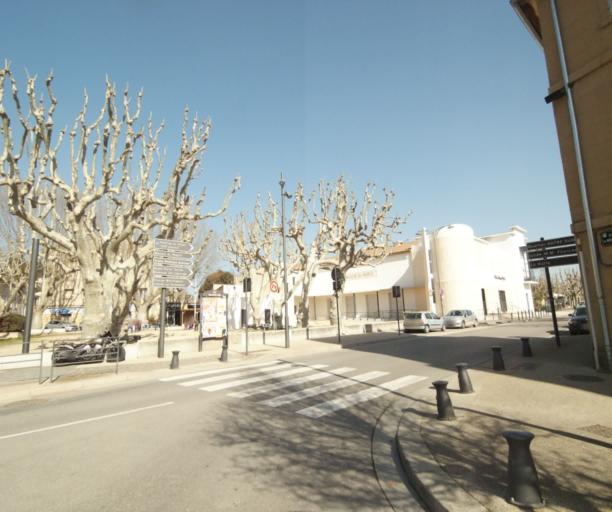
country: FR
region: Provence-Alpes-Cote d'Azur
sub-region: Departement des Bouches-du-Rhone
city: Gardanne
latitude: 43.4564
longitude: 5.4719
